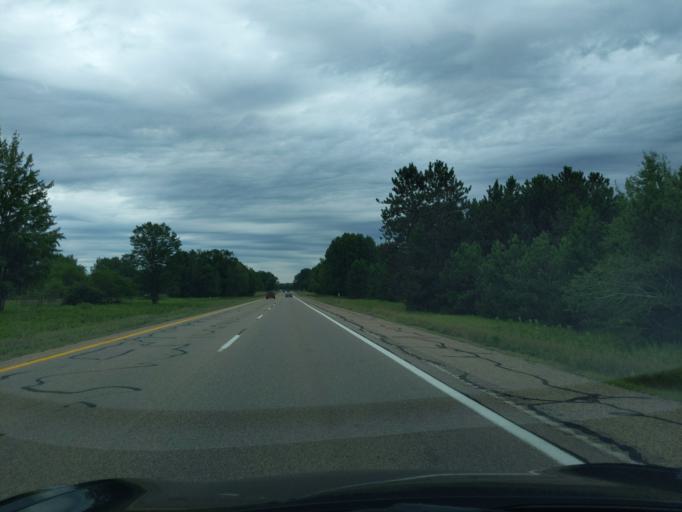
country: US
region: Michigan
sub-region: Roscommon County
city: Houghton Lake
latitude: 44.3200
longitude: -84.8070
